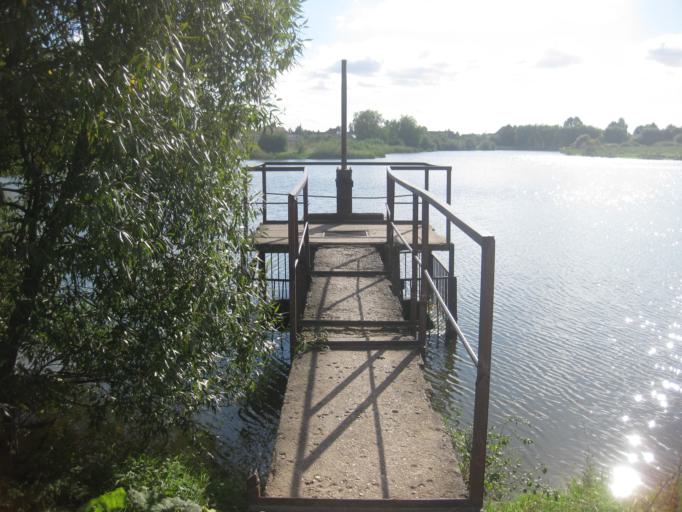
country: LT
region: Kauno apskritis
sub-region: Kauno rajonas
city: Garliava
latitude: 54.8287
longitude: 23.8691
